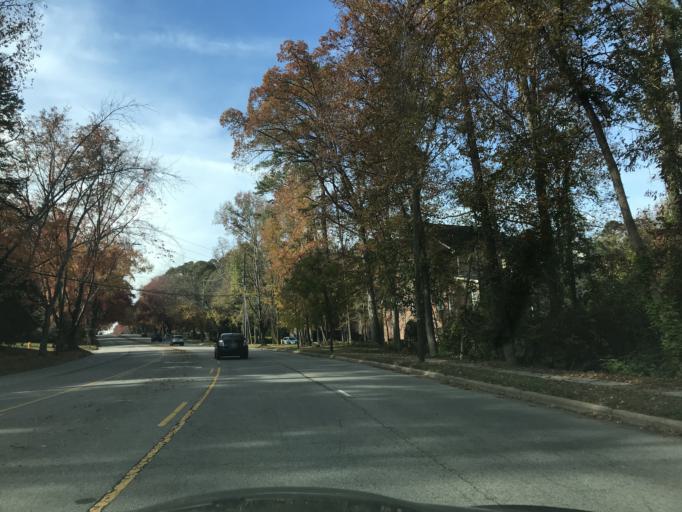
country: US
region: North Carolina
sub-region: Wake County
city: West Raleigh
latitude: 35.8515
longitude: -78.6231
